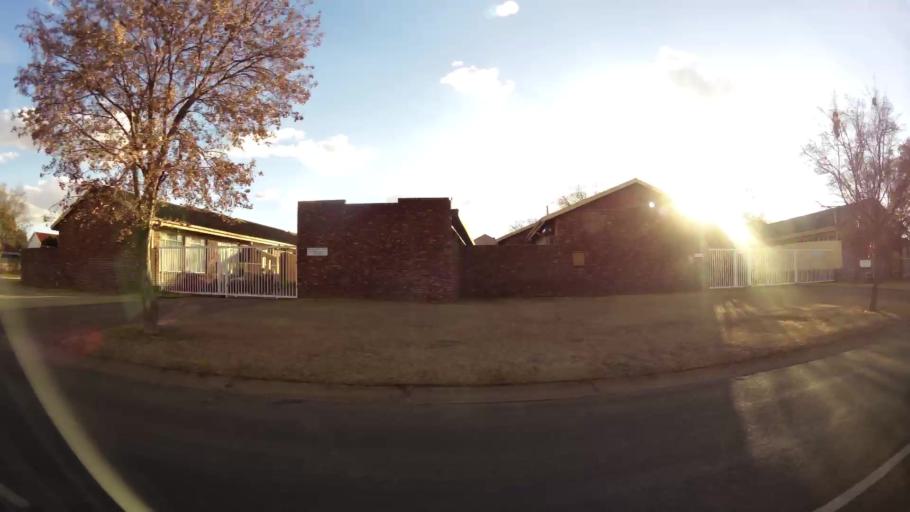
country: ZA
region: North-West
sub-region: Dr Kenneth Kaunda District Municipality
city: Potchefstroom
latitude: -26.7317
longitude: 27.0998
